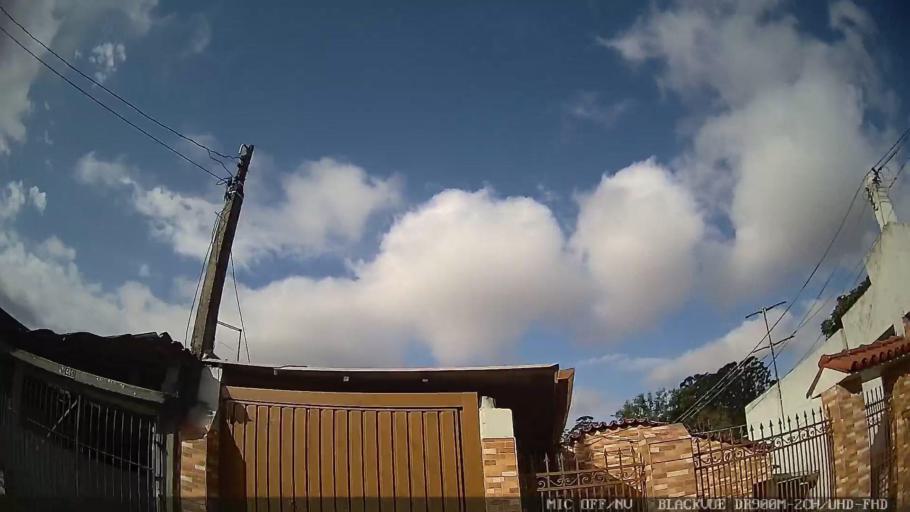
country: BR
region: Sao Paulo
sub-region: Sao Caetano Do Sul
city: Sao Caetano do Sul
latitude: -23.5703
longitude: -46.5332
